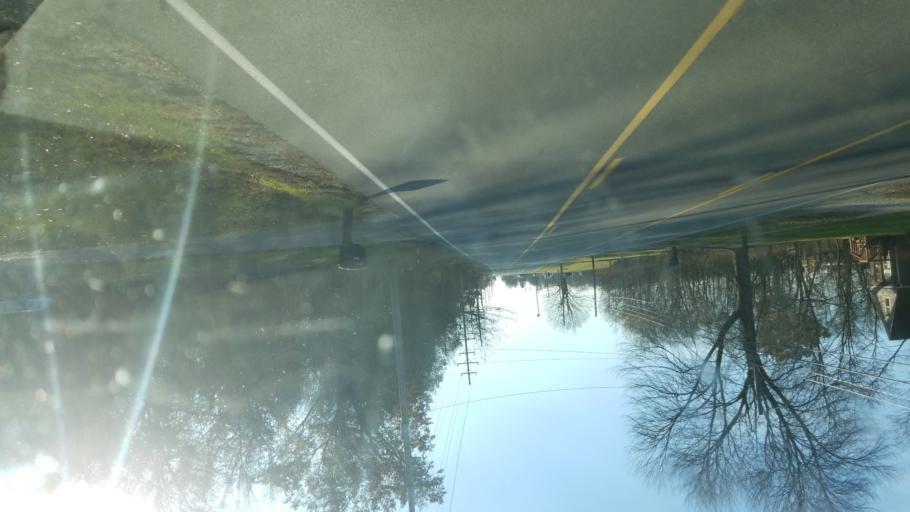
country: US
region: Ohio
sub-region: Summit County
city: Tallmadge
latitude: 41.0898
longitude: -81.4414
